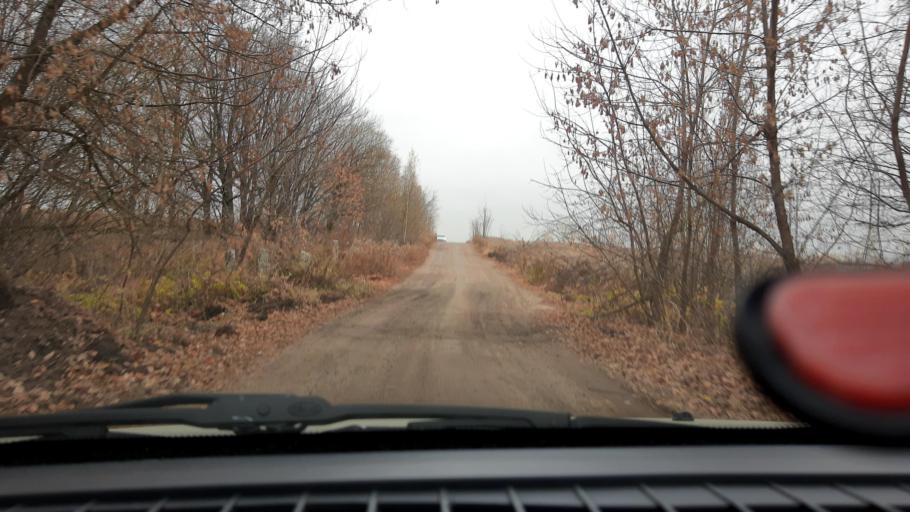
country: RU
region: Nizjnij Novgorod
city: Afonino
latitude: 56.2550
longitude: 44.0475
